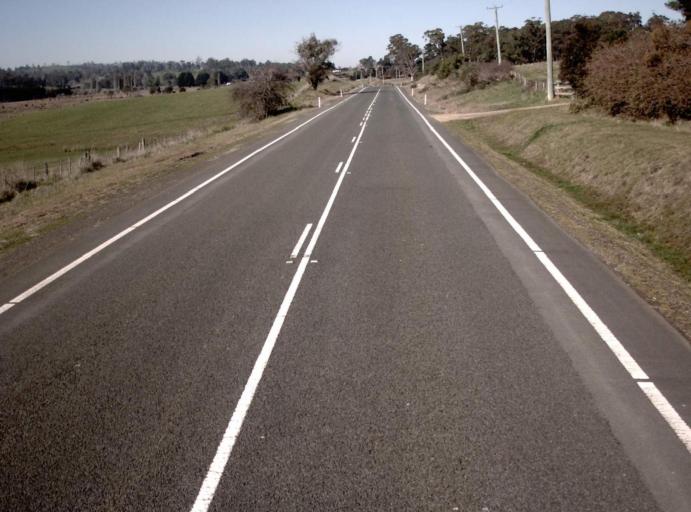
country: AU
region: Tasmania
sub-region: Launceston
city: Mayfield
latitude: -41.3197
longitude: 147.0590
